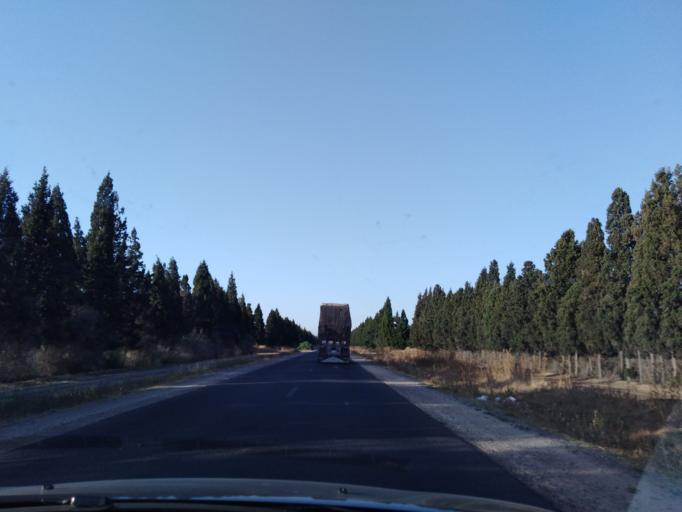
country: MA
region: Doukkala-Abda
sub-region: Safi
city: Safi
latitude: 32.5019
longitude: -8.9242
